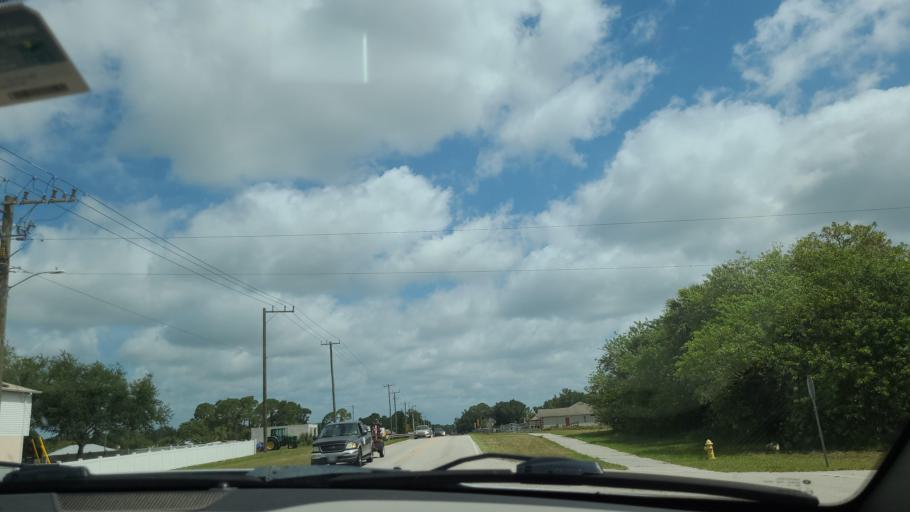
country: US
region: Florida
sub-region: Brevard County
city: June Park
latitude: 28.0125
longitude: -80.6967
